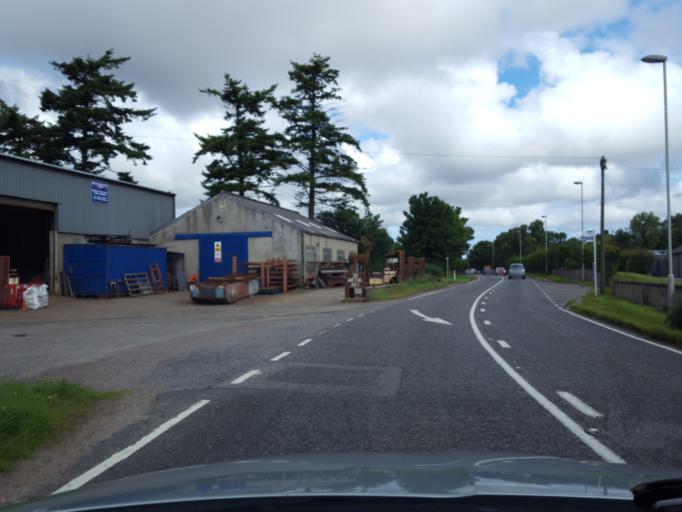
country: GB
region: Scotland
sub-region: Moray
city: Lhanbryd
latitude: 57.5947
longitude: -3.2808
